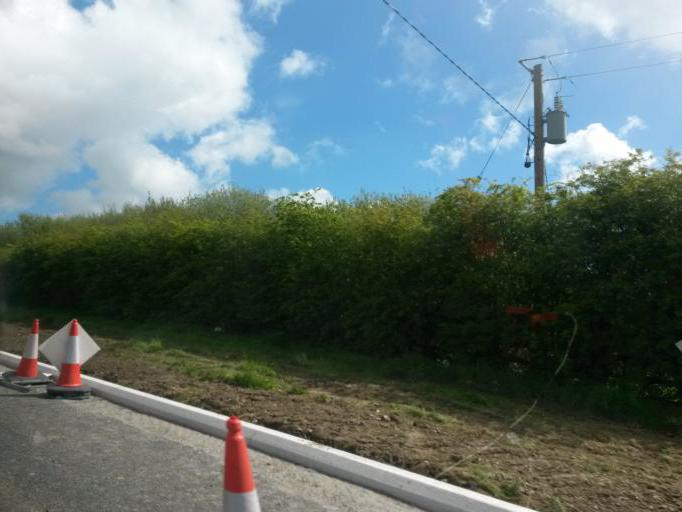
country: IE
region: Leinster
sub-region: Loch Garman
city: Castlebridge
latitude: 52.3832
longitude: -6.5184
